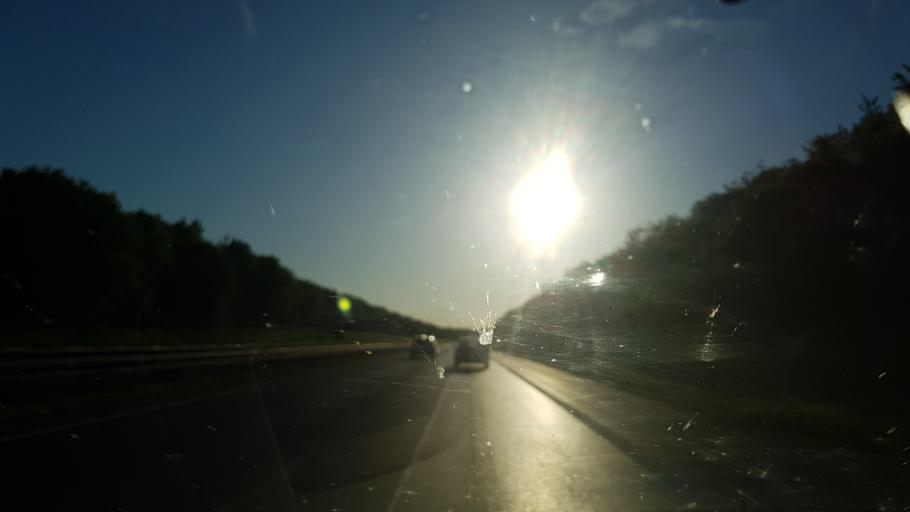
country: DE
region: North Rhine-Westphalia
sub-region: Regierungsbezirk Dusseldorf
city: Bruggen
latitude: 51.2073
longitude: 6.1578
